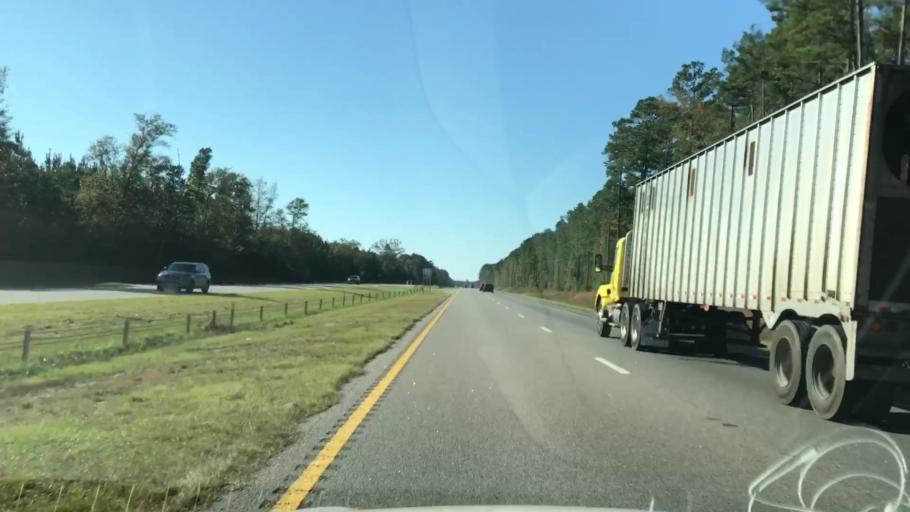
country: US
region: South Carolina
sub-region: Colleton County
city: Walterboro
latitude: 32.6919
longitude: -80.6275
